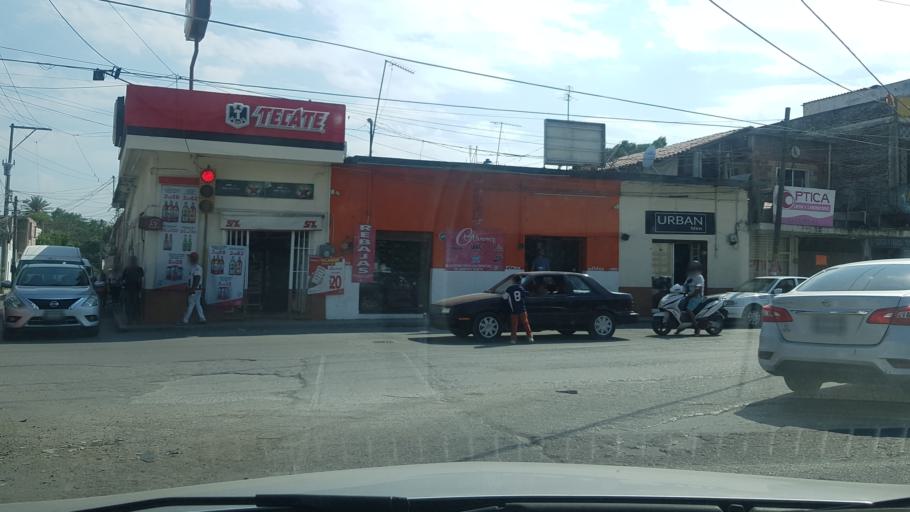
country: MX
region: Morelos
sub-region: Jojutla
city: Jojutla
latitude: 18.6162
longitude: -99.1826
